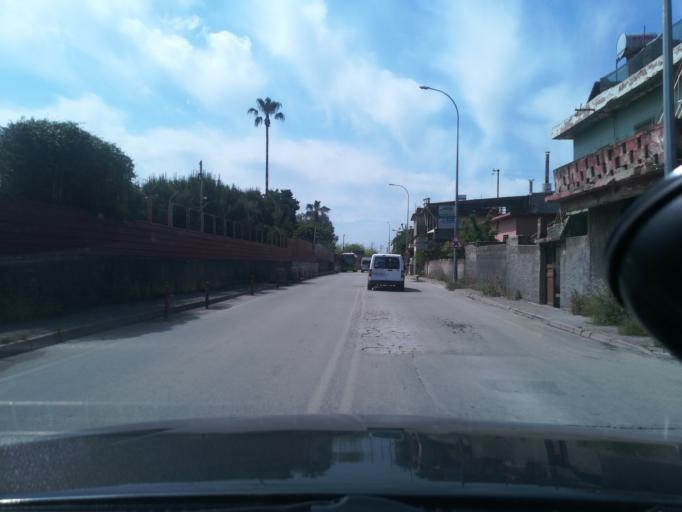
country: TR
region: Adana
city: Seyhan
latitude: 36.9893
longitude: 35.2866
